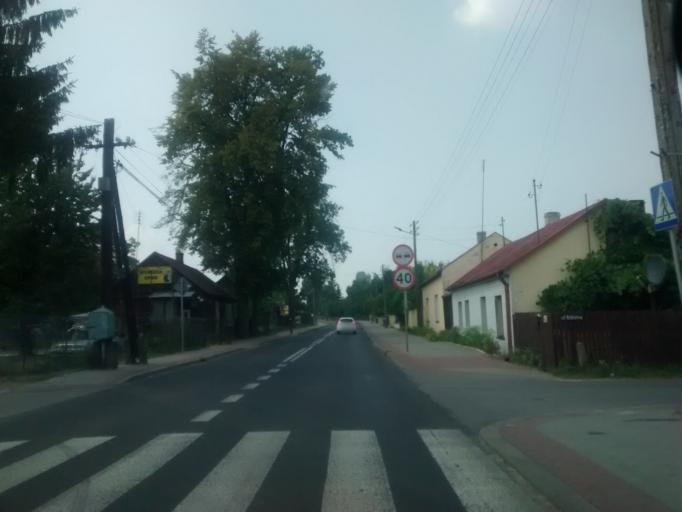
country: PL
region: Silesian Voivodeship
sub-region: Powiat czestochowski
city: Potok Zloty
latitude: 50.7229
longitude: 19.4328
